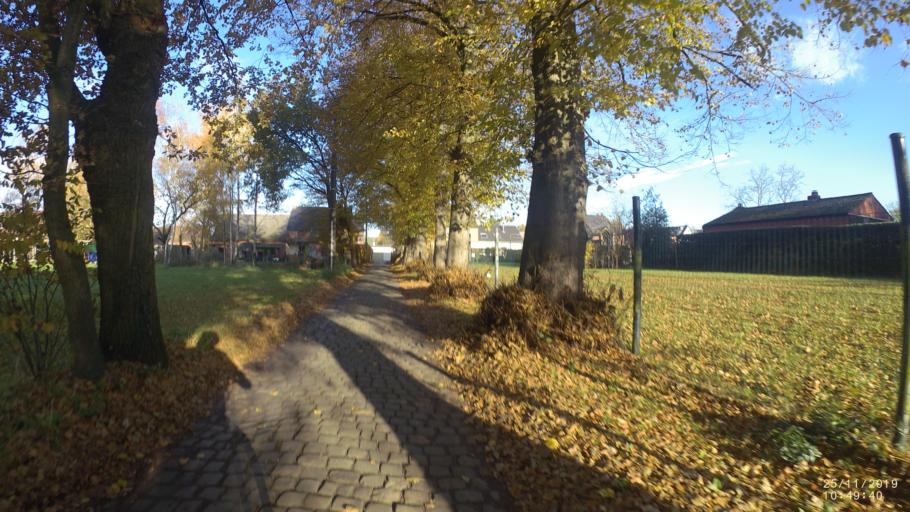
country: BE
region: Flanders
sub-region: Provincie Vlaams-Brabant
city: Scherpenheuvel-Zichem
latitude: 51.0111
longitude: 4.9343
